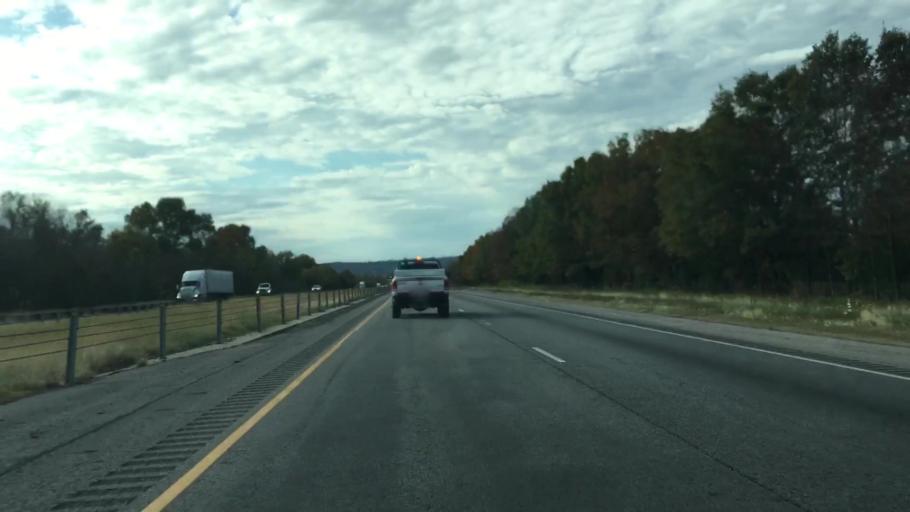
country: US
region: Arkansas
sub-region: Pope County
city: Atkins
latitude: 35.2478
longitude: -92.8726
